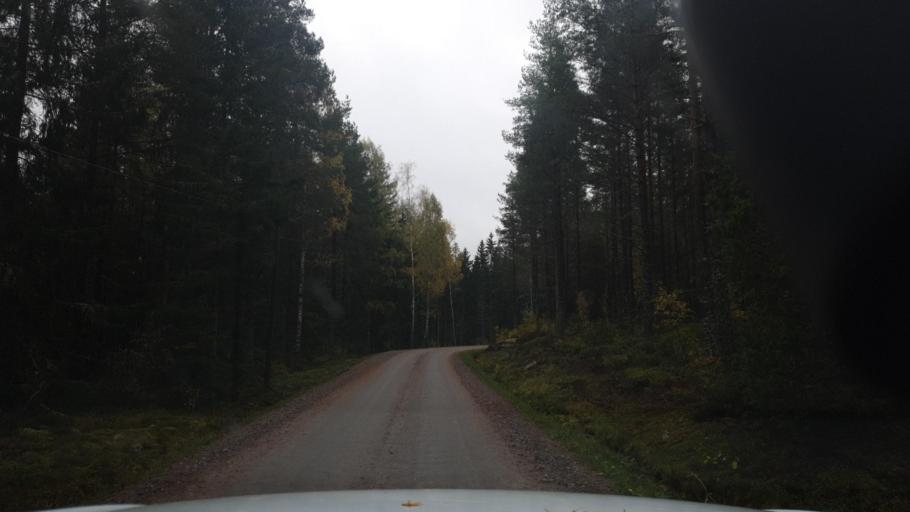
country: SE
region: Vaermland
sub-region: Karlstads Kommun
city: Edsvalla
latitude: 59.5379
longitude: 12.9975
